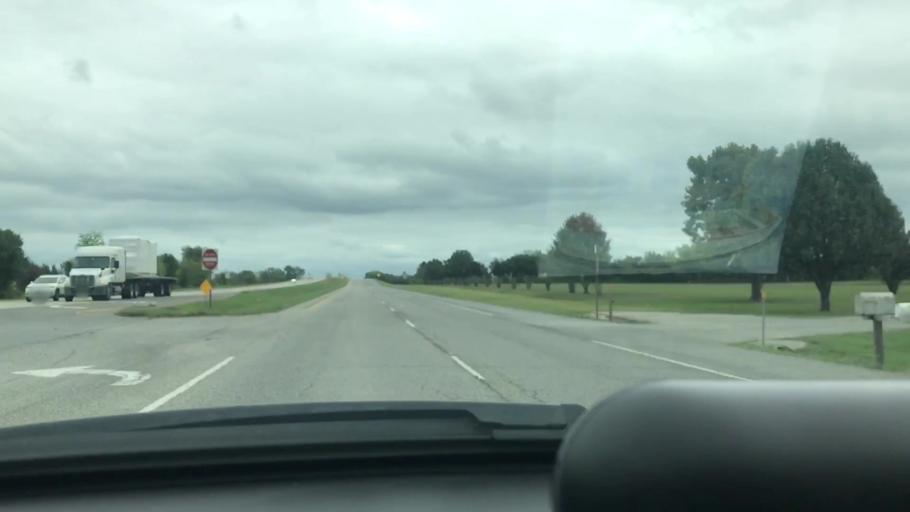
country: US
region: Oklahoma
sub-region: Wagoner County
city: Wagoner
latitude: 35.9748
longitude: -95.3844
